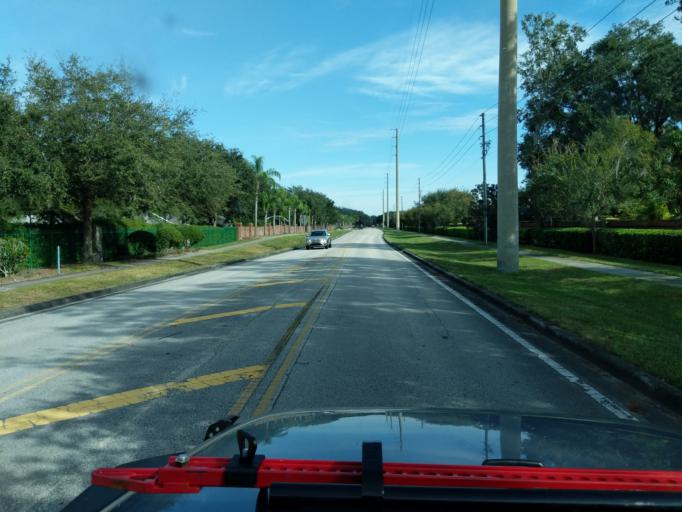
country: US
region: Florida
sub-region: Orange County
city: Gotha
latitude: 28.5298
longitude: -81.5384
